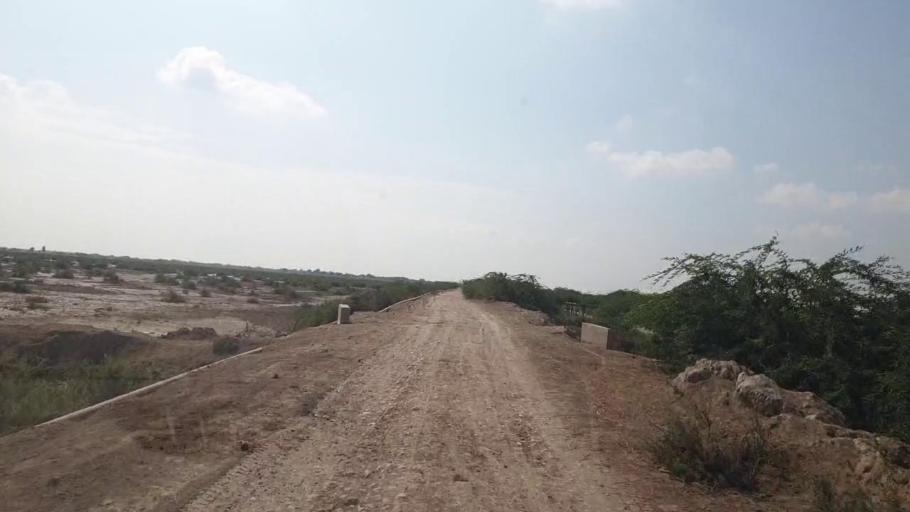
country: PK
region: Sindh
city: Badin
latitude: 24.5010
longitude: 68.6074
